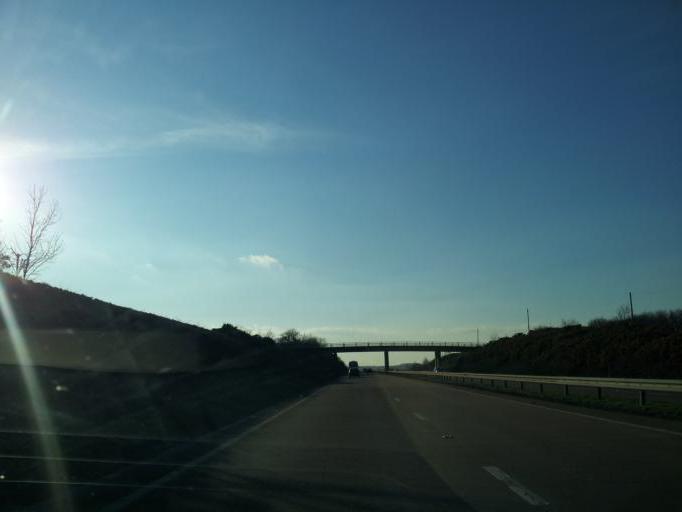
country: GB
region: England
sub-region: Devon
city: Okehampton
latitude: 50.7314
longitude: -3.8807
